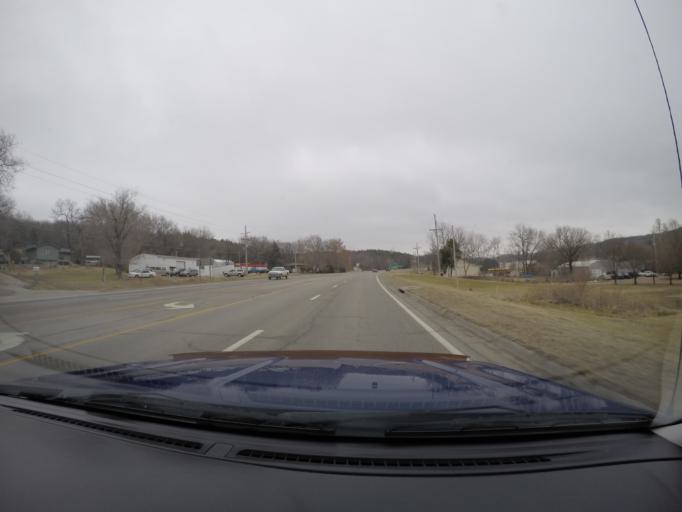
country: US
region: Kansas
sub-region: Riley County
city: Manhattan
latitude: 39.1704
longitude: -96.5432
